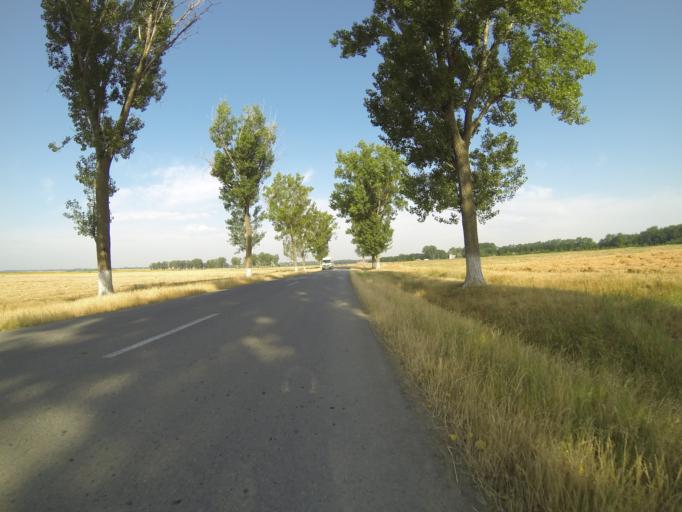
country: RO
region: Dolj
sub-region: Comuna Valea Stanciului
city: Valea Stanciului
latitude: 43.9817
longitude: 23.9014
